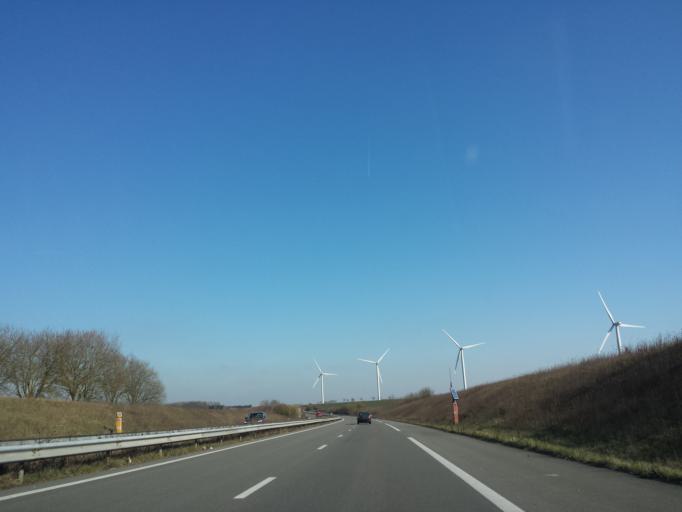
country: FR
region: Picardie
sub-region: Departement de l'Oise
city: Breteuil
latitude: 49.6875
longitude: 2.2250
